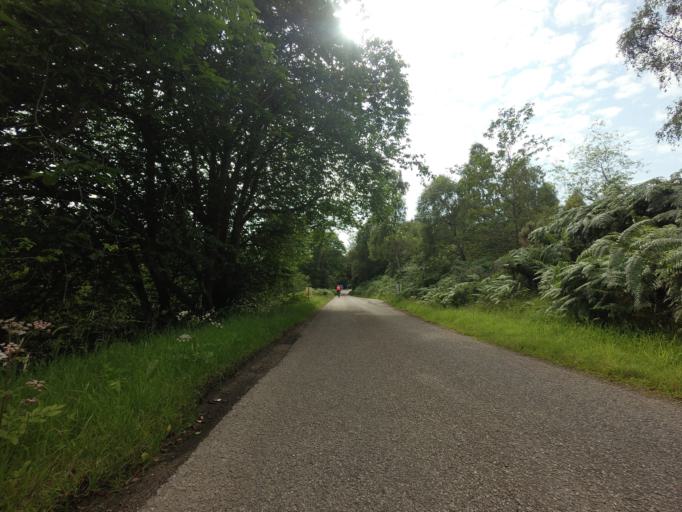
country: GB
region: Scotland
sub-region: Highland
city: Evanton
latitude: 57.9454
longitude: -4.4082
